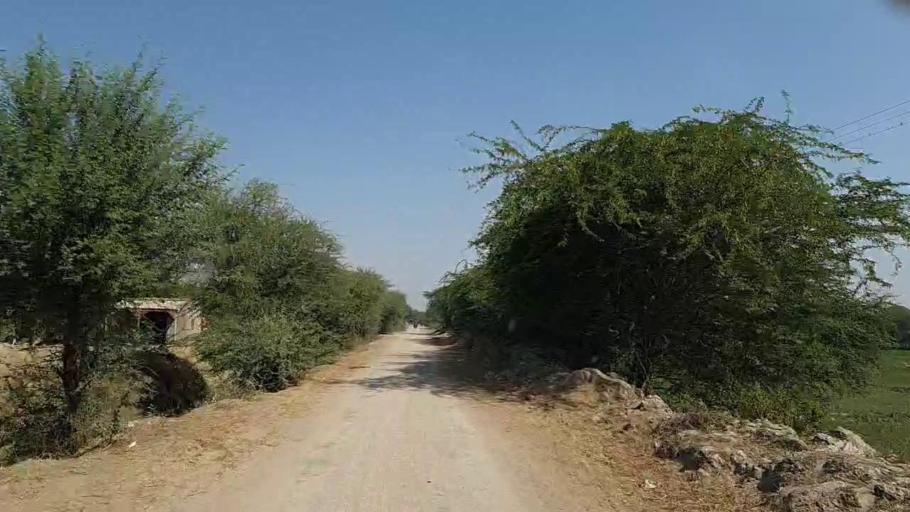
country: PK
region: Sindh
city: Mirpur Batoro
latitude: 24.6897
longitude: 68.2577
